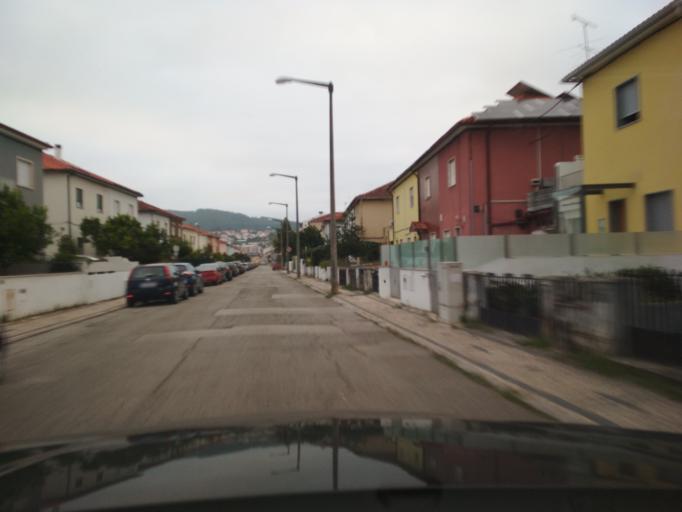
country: PT
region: Coimbra
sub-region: Coimbra
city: Coimbra
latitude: 40.1976
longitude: -8.4096
